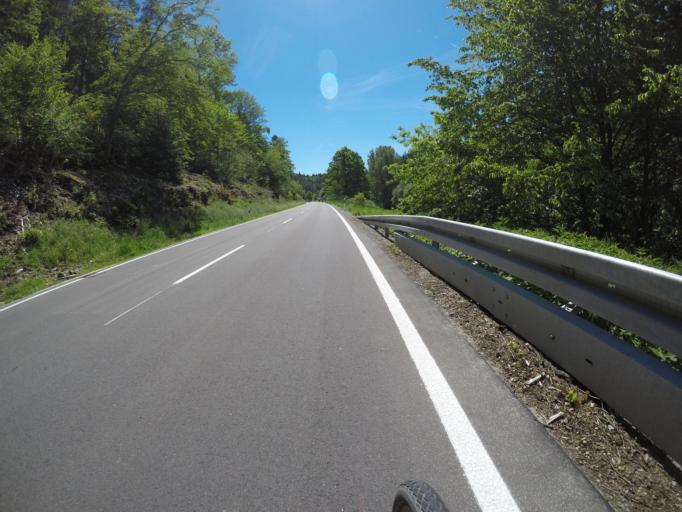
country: DE
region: Baden-Wuerttemberg
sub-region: Karlsruhe Region
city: Tiefenbronn
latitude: 48.8151
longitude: 8.8018
